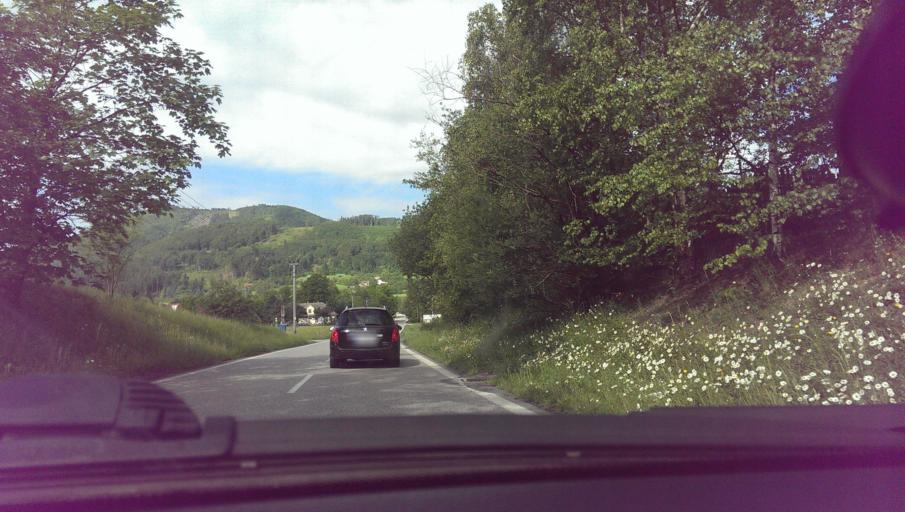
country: CZ
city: Trojanovice
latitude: 49.5161
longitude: 18.2086
